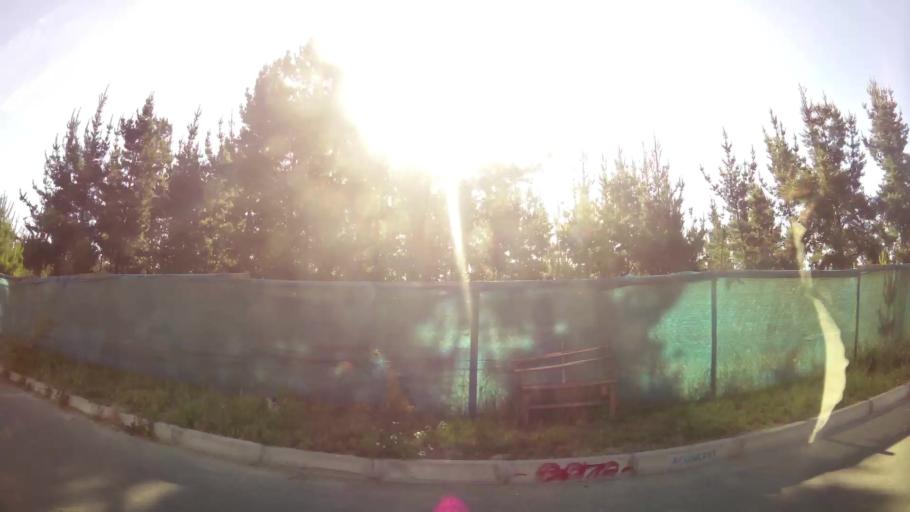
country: CL
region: Valparaiso
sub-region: Provincia de Valparaiso
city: Valparaiso
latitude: -33.1200
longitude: -71.5857
